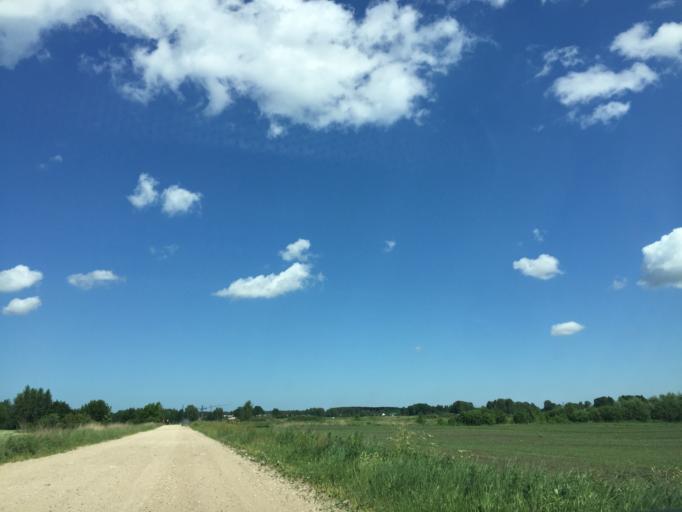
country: LV
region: Olaine
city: Olaine
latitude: 56.8676
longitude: 23.9555
